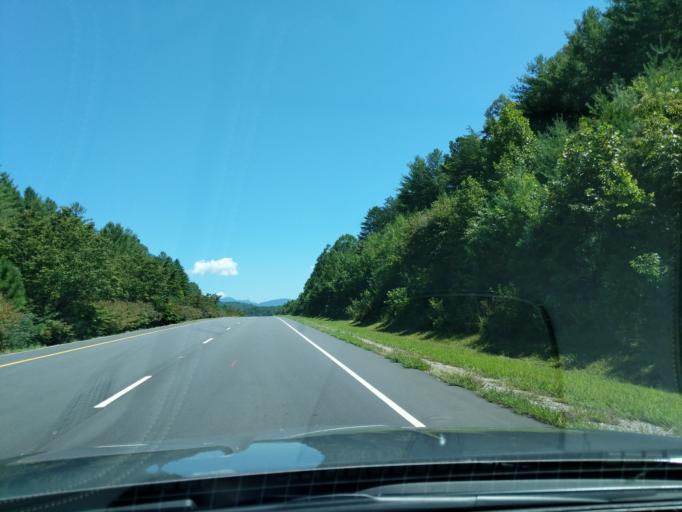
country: US
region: North Carolina
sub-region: Macon County
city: Franklin
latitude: 35.1611
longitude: -83.4463
